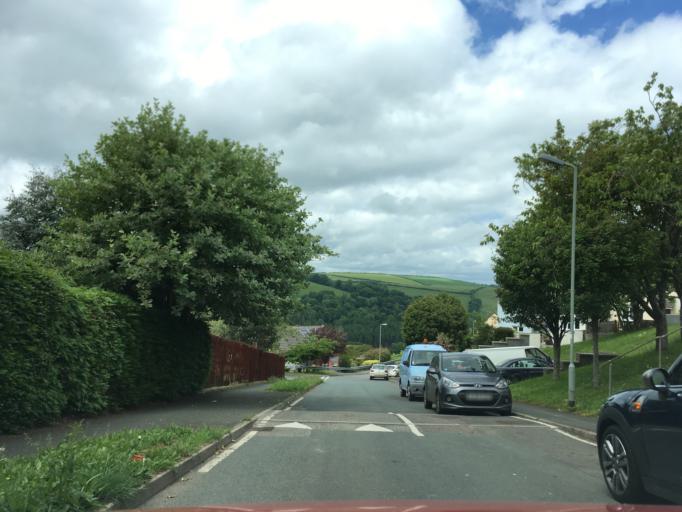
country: GB
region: England
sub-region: Devon
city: Dartmouth
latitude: 50.3542
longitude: -3.5929
